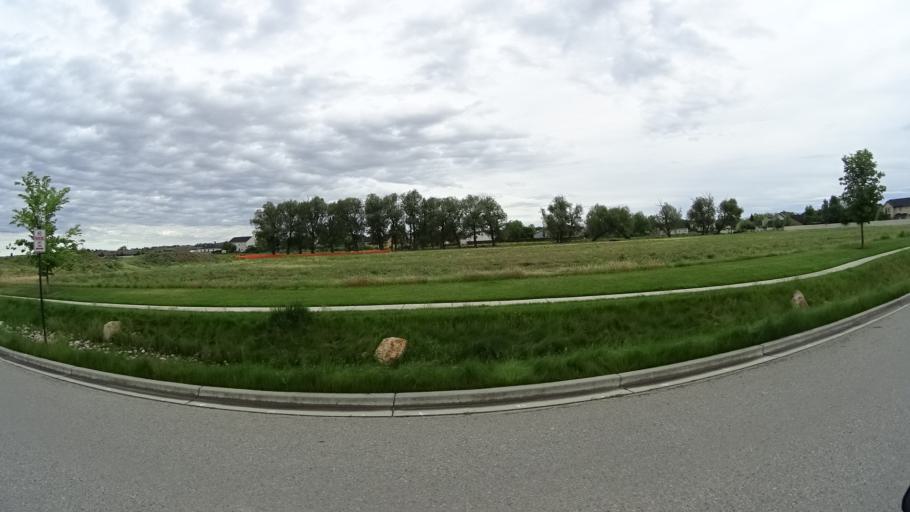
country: US
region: Idaho
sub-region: Ada County
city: Star
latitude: 43.7012
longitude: -116.4965
